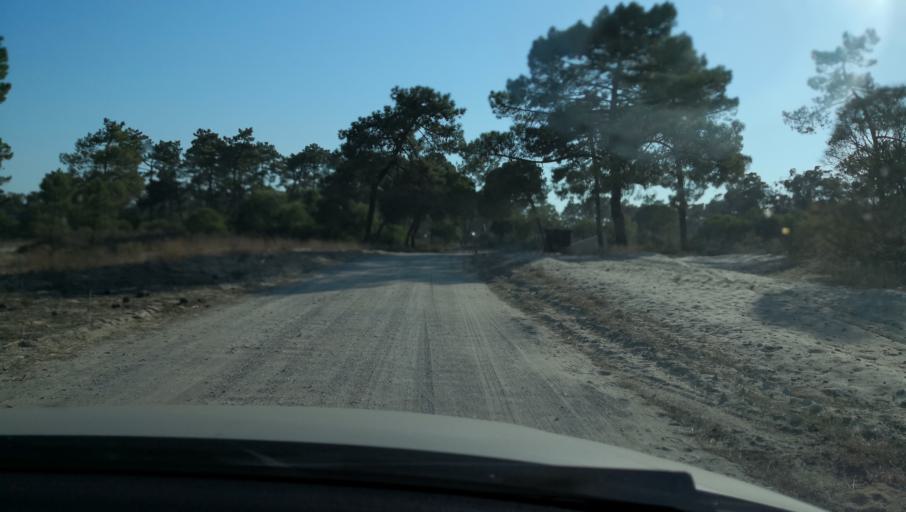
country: PT
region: Setubal
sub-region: Setubal
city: Setubal
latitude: 38.4671
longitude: -8.8740
